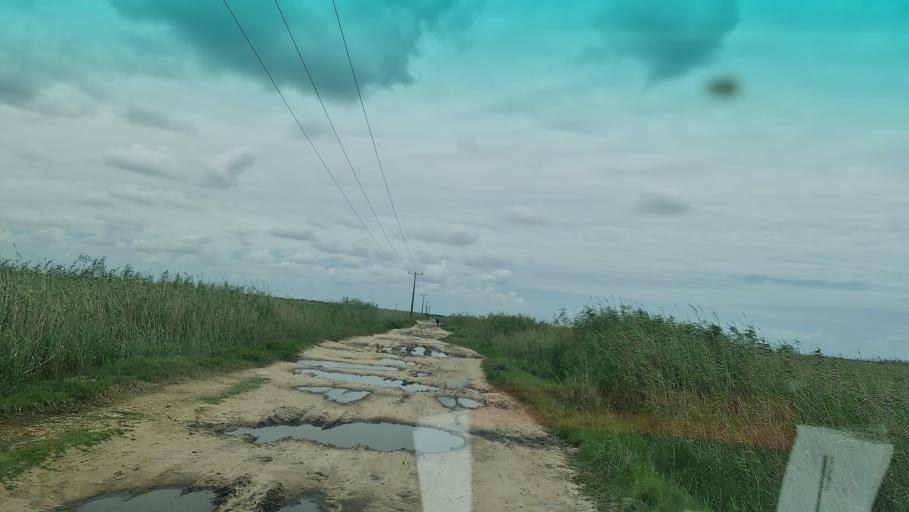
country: MZ
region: Maputo City
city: Maputo
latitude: -25.7194
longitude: 32.7002
